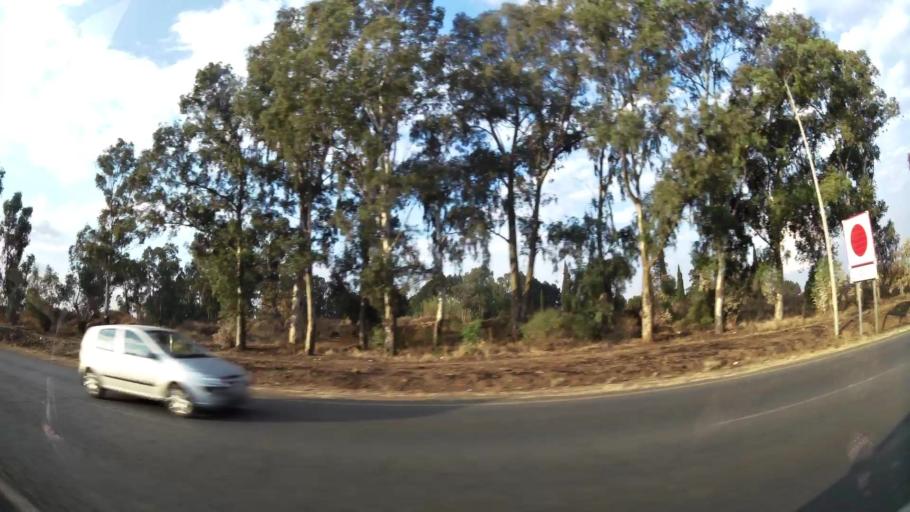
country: ZA
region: Gauteng
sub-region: Sedibeng District Municipality
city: Vanderbijlpark
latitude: -26.6967
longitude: 27.8077
